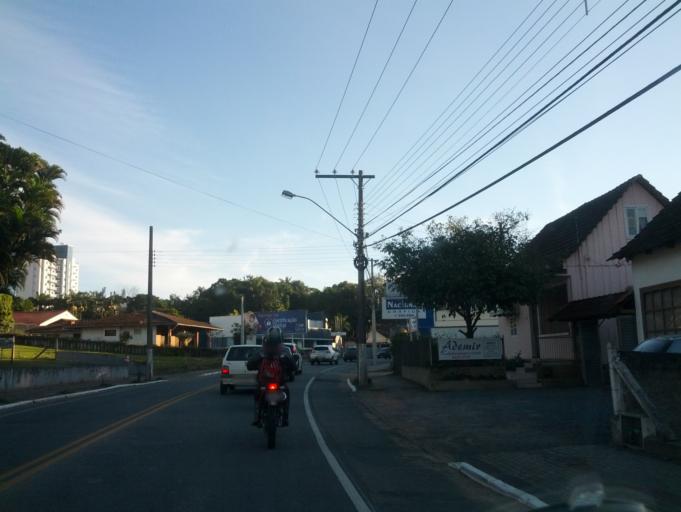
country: BR
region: Santa Catarina
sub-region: Indaial
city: Indaial
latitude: -26.8938
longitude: -49.2274
